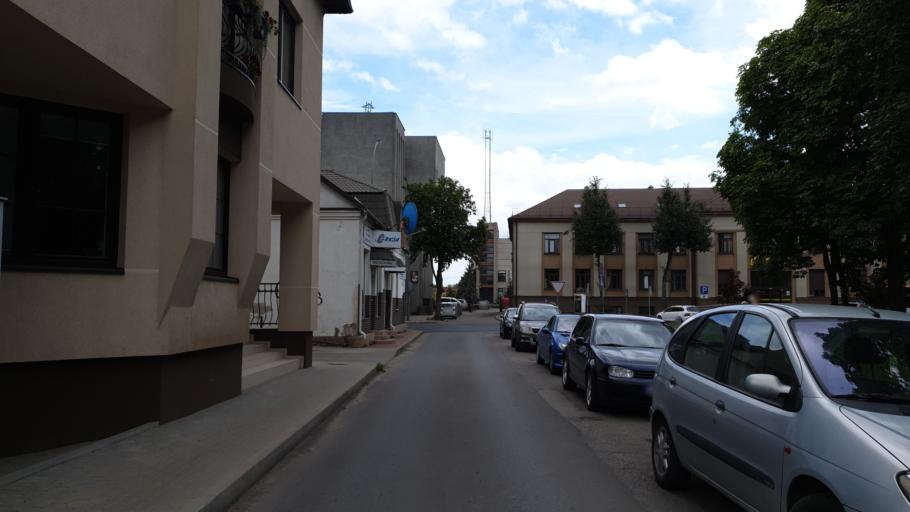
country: LT
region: Panevezys
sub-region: Panevezys City
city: Panevezys
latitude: 55.7346
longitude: 24.3567
